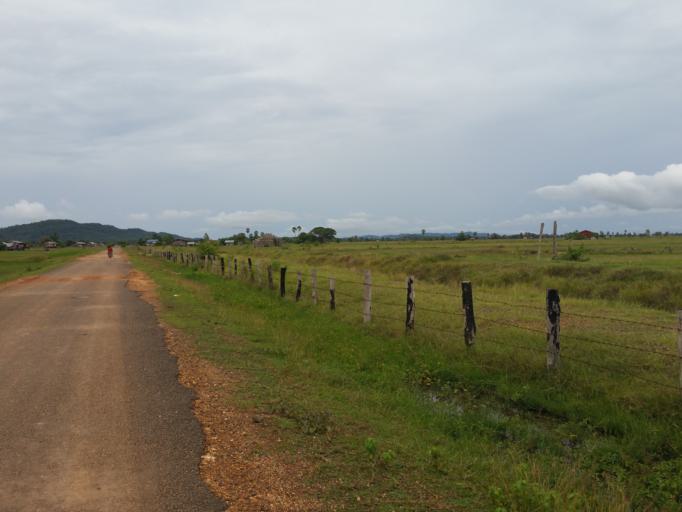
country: LA
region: Champasak
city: Khong
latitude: 14.1079
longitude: 105.8023
